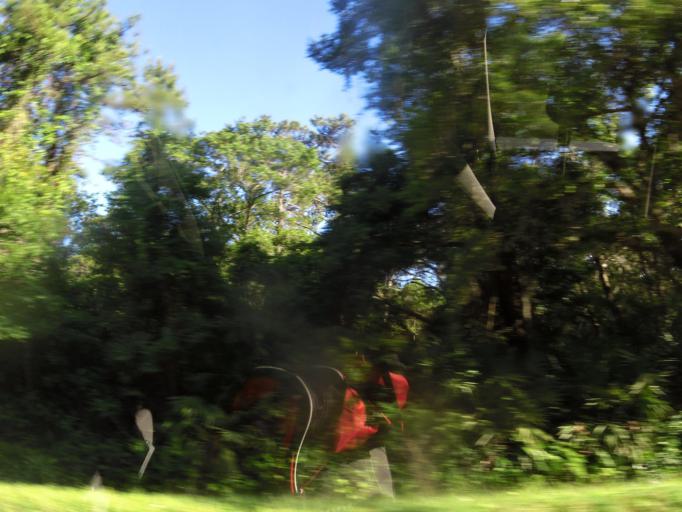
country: US
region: Florida
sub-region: Duval County
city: Atlantic Beach
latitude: 30.4621
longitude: -81.4934
